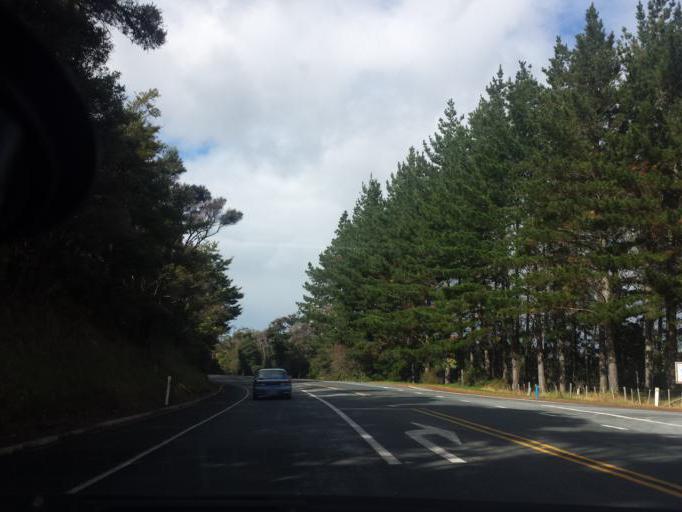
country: NZ
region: Auckland
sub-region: Auckland
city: Warkworth
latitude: -36.4002
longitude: 174.6952
